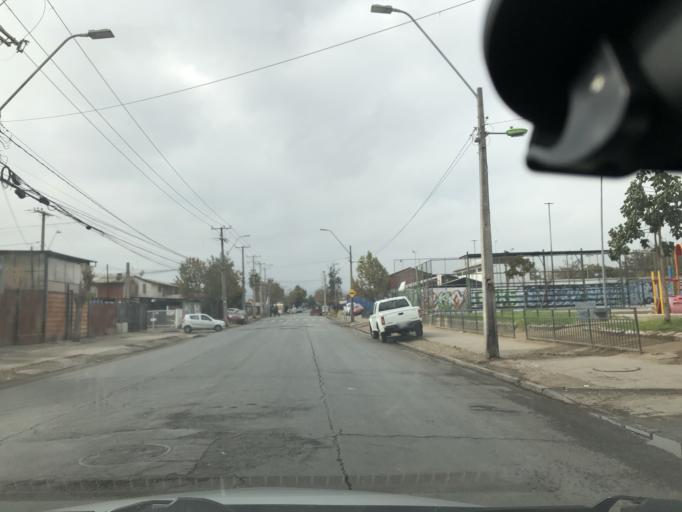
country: CL
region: Santiago Metropolitan
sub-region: Provincia de Santiago
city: La Pintana
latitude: -33.5888
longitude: -70.6044
